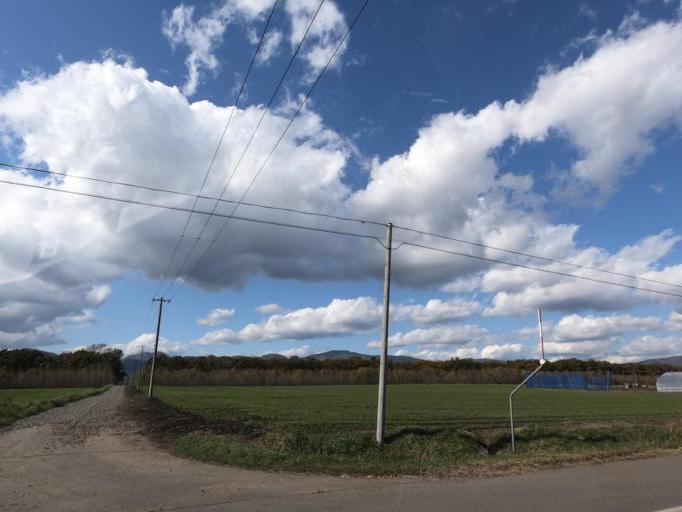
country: JP
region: Hokkaido
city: Otofuke
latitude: 43.2366
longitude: 143.2543
